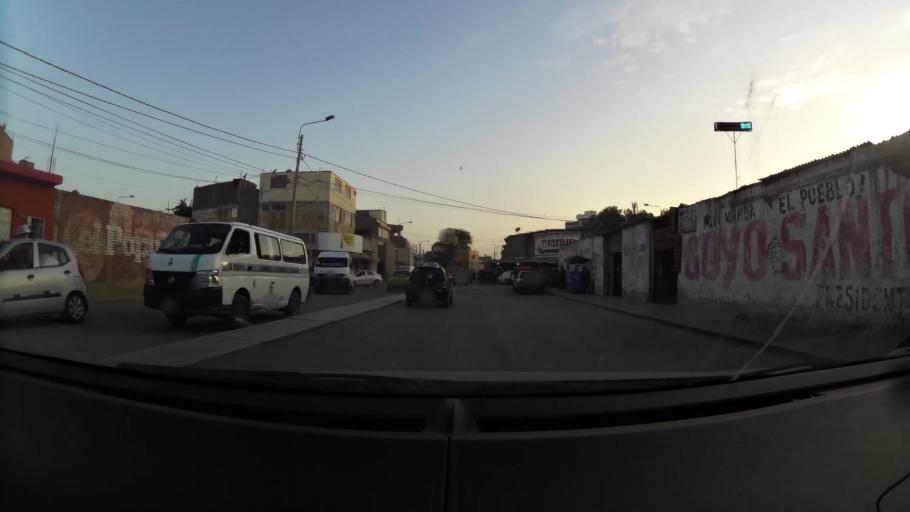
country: PE
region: Lambayeque
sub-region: Provincia de Chiclayo
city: Santa Rosa
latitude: -6.7646
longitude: -79.8318
